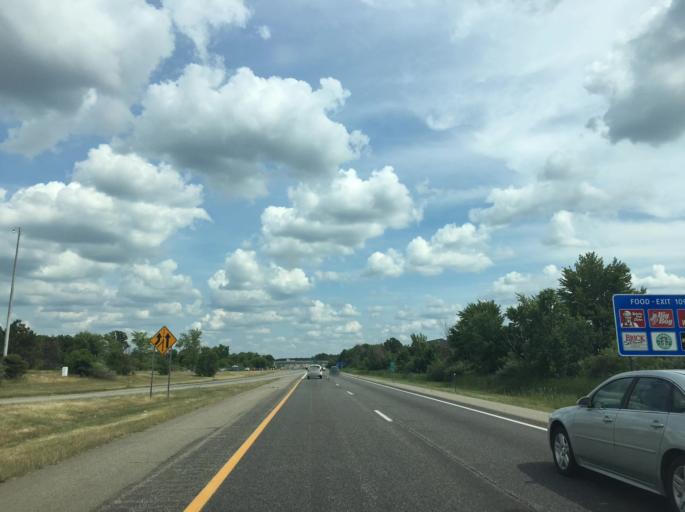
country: US
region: Michigan
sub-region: Genesee County
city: Grand Blanc
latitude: 42.9190
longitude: -83.6796
